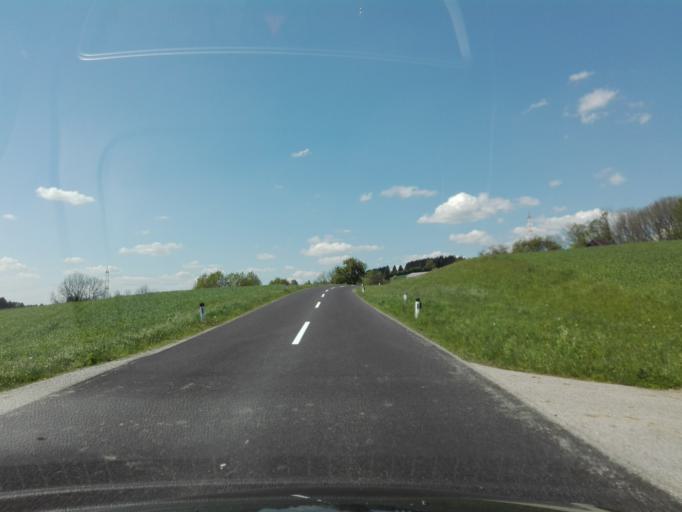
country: AT
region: Upper Austria
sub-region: Politischer Bezirk Rohrbach
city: Kleinzell im Muehlkreis
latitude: 48.3583
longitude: 13.9378
